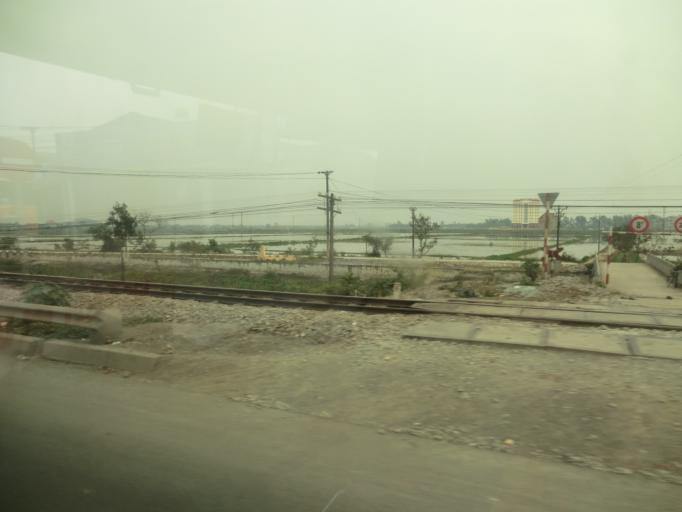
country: VN
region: Ha Nam
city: Thanh Pho Phu Ly
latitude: 20.5580
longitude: 105.9199
